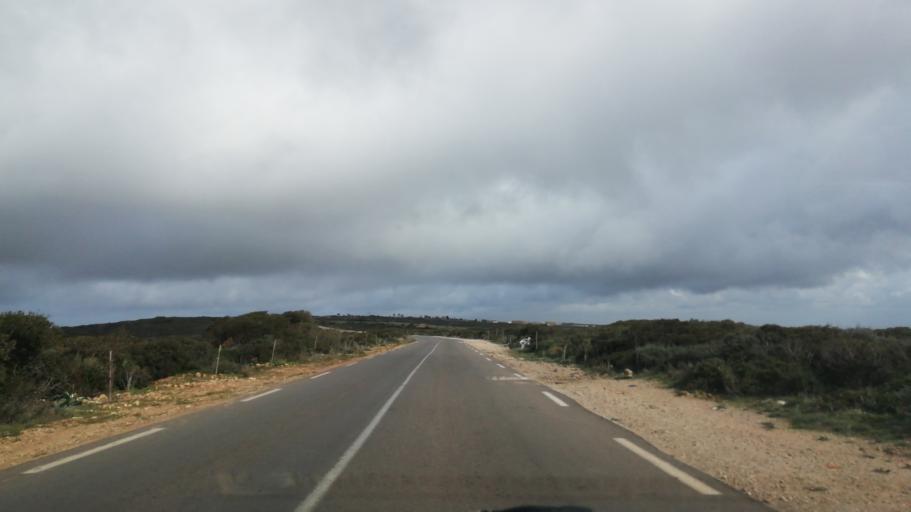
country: DZ
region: Oran
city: Mers el Kebir
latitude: 35.7017
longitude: -0.7424
